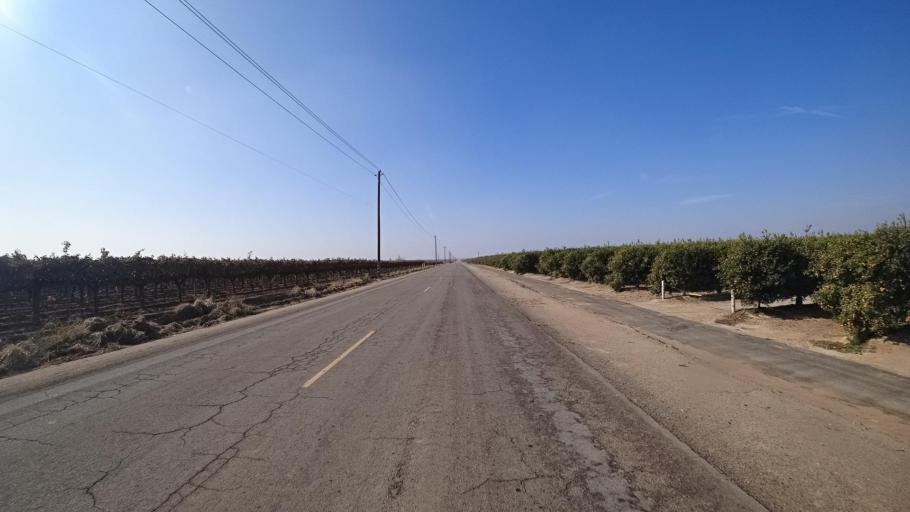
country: US
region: California
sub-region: Kern County
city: Greenacres
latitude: 35.5299
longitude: -119.1210
